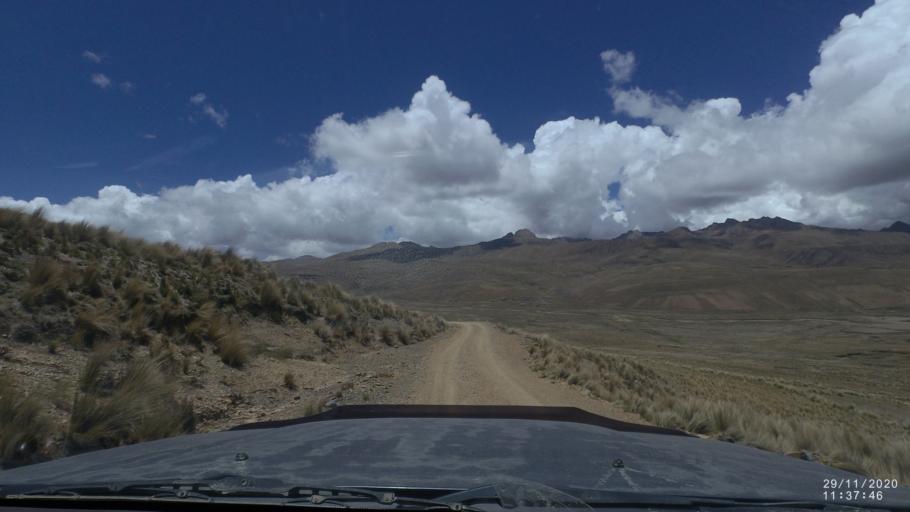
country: BO
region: Cochabamba
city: Cochabamba
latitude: -17.1979
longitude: -66.2341
